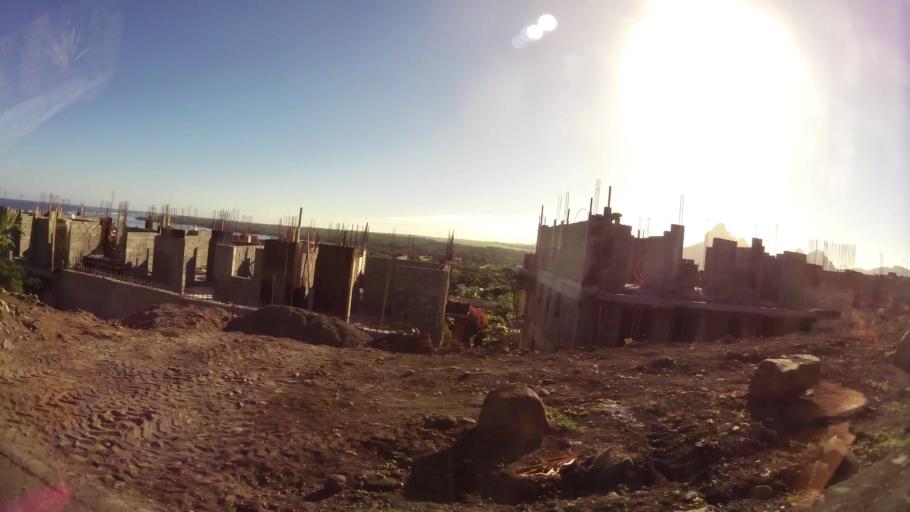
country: MU
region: Black River
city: Tamarin
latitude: -20.3395
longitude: 57.3778
